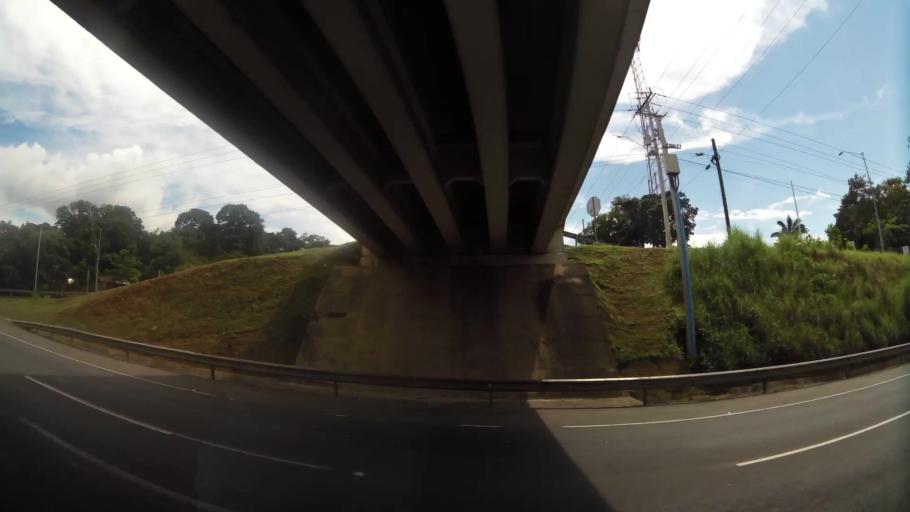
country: PA
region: Panama
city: Vista Alegre
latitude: 8.9320
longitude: -79.6848
